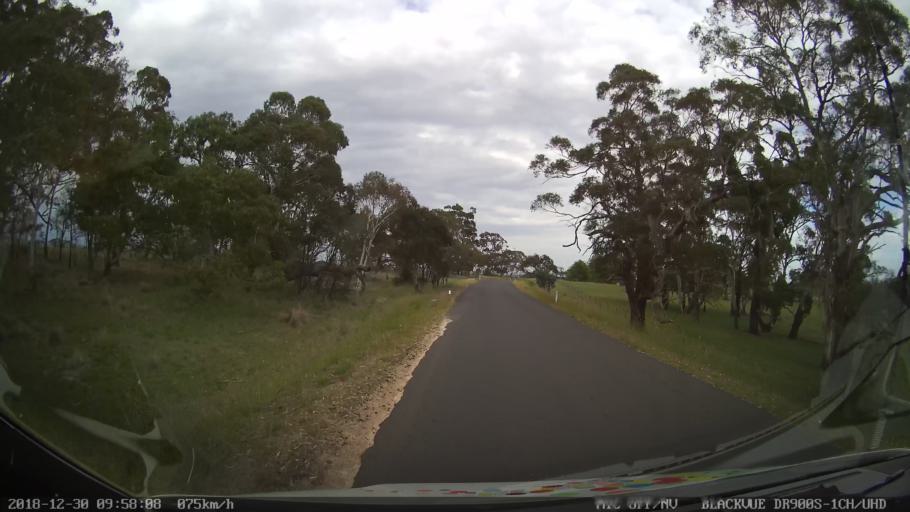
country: AU
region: New South Wales
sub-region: Cooma-Monaro
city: Cooma
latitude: -36.5223
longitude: 149.2303
